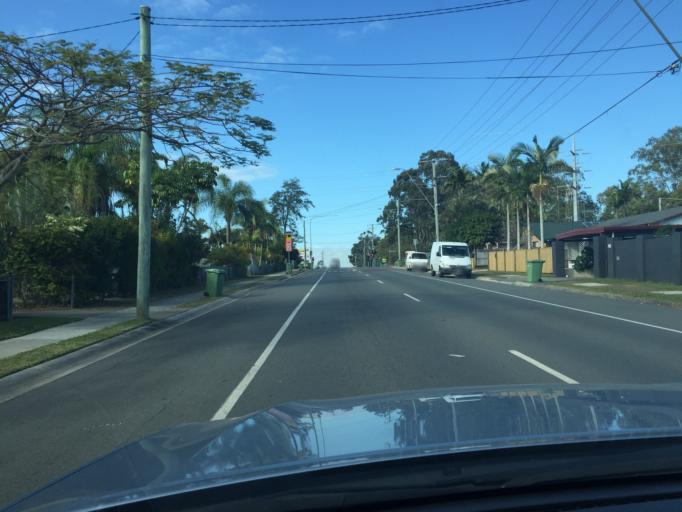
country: AU
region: Queensland
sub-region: Logan
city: Slacks Creek
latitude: -27.6418
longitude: 153.1538
